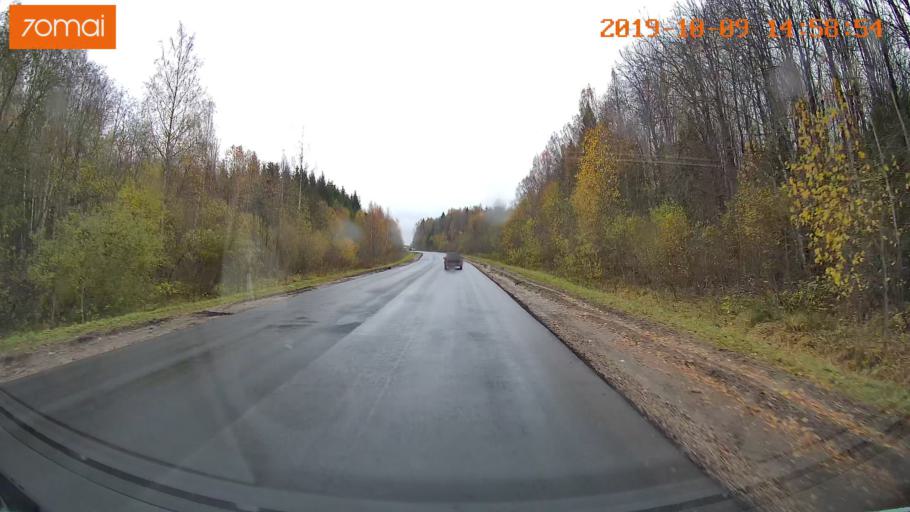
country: RU
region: Kostroma
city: Chistyye Bory
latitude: 58.3233
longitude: 41.6593
